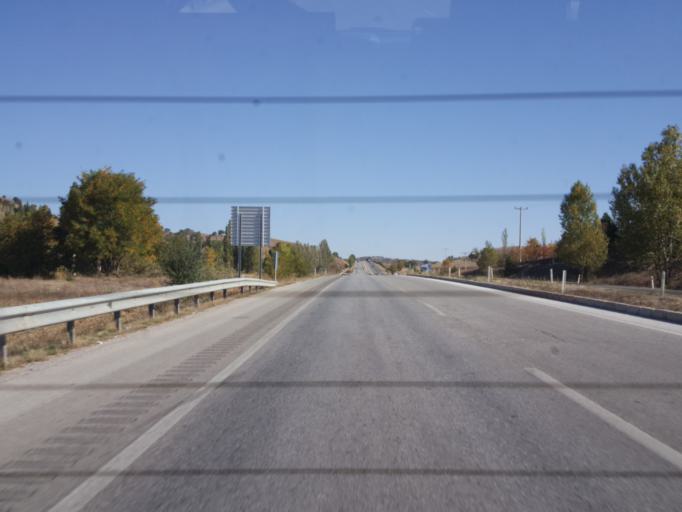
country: TR
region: Corum
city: Alaca
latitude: 40.2792
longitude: 34.6443
